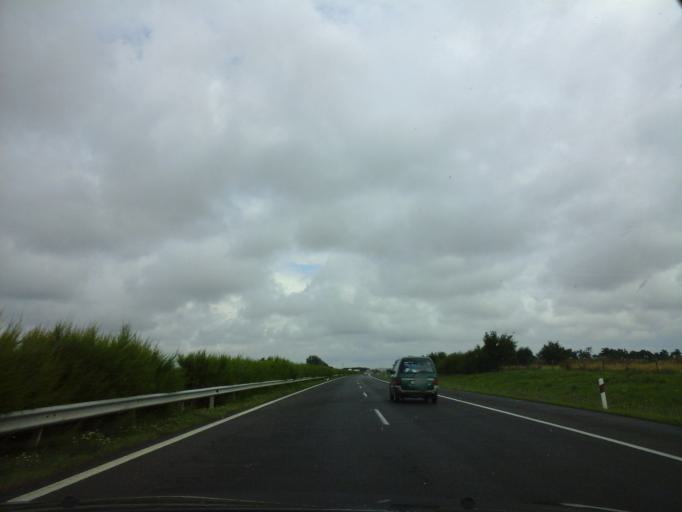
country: HU
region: Borsod-Abauj-Zemplen
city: Emod
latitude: 47.9089
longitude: 20.8395
